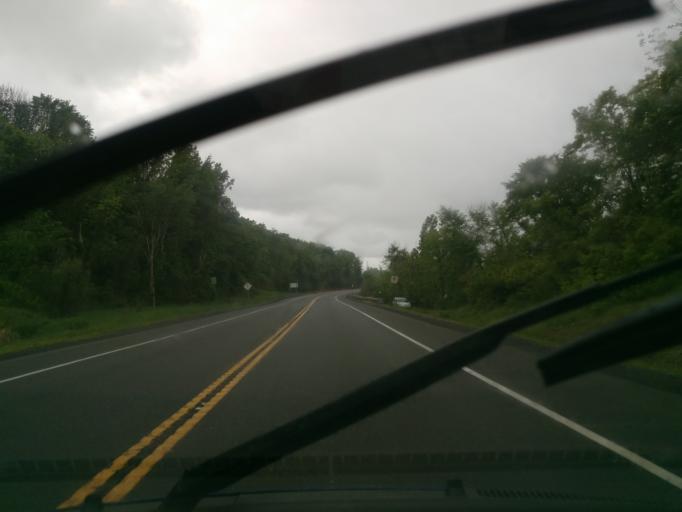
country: CA
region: Ontario
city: Clarence-Rockland
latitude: 45.5124
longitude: -75.4620
